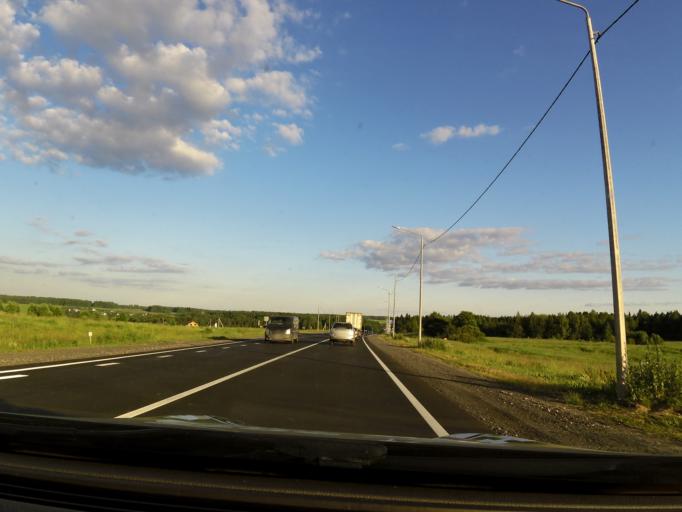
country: RU
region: Vologda
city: Gryazovets
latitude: 59.0365
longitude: 40.1078
